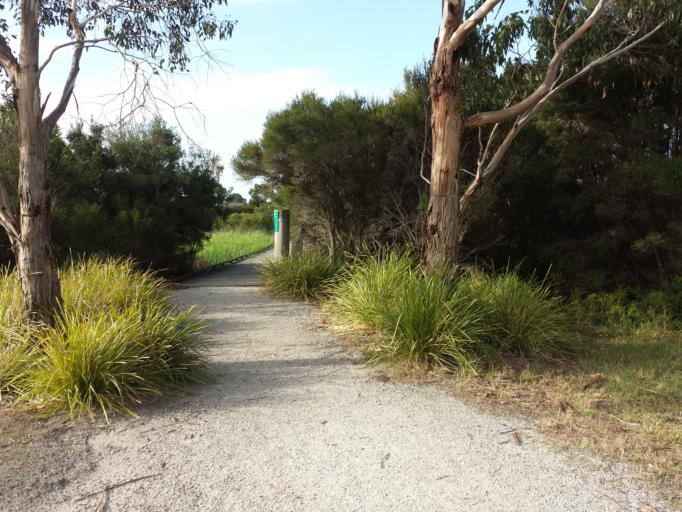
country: AU
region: Victoria
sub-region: Monash
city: Oakleigh South
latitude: -37.9415
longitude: 145.0810
